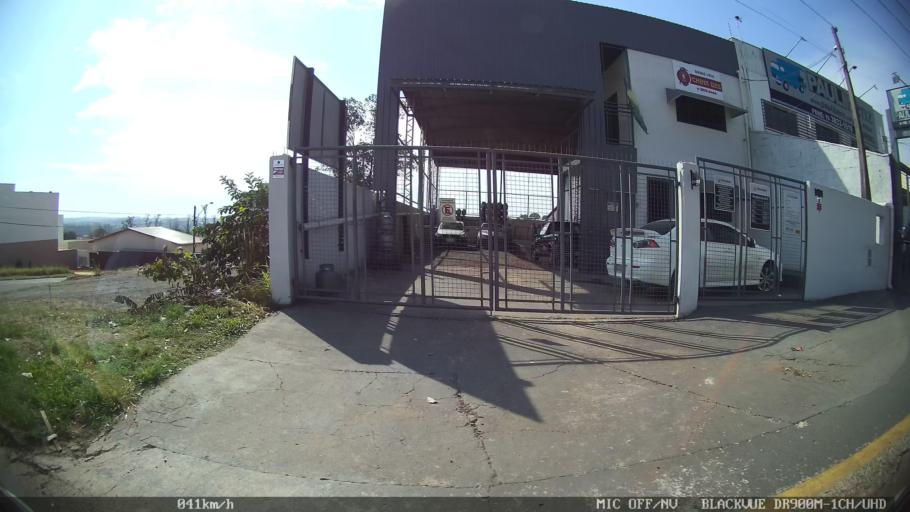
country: BR
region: Sao Paulo
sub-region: Paulinia
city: Paulinia
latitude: -22.7812
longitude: -47.1607
